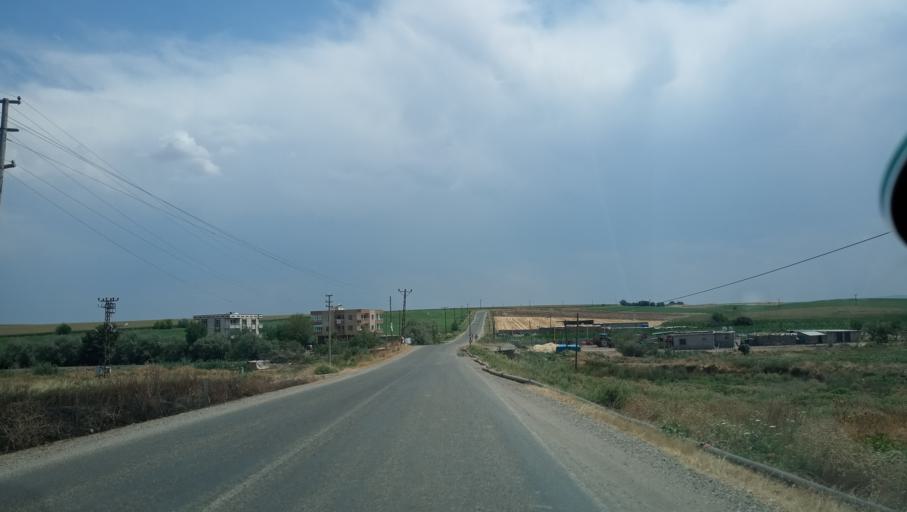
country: TR
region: Diyarbakir
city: Tepe
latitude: 37.7585
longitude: 40.8184
